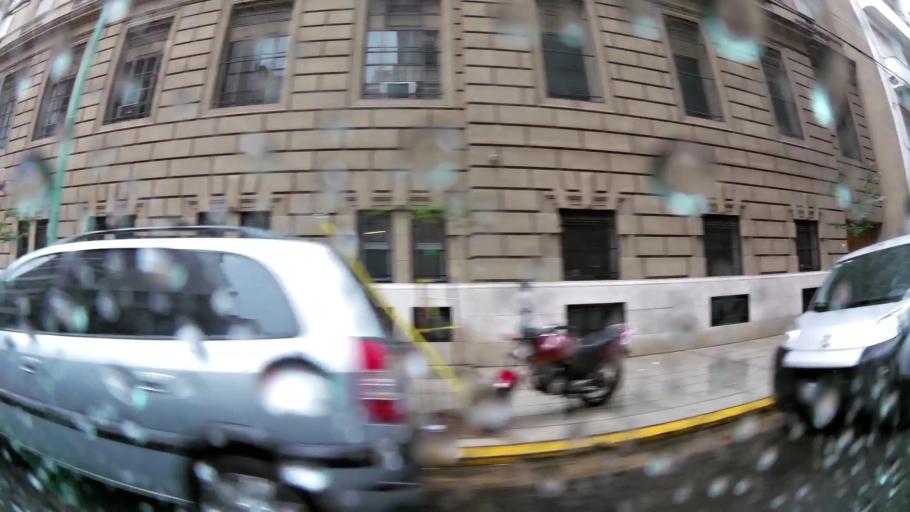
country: AR
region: Buenos Aires F.D.
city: Retiro
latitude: -34.5963
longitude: -58.3900
